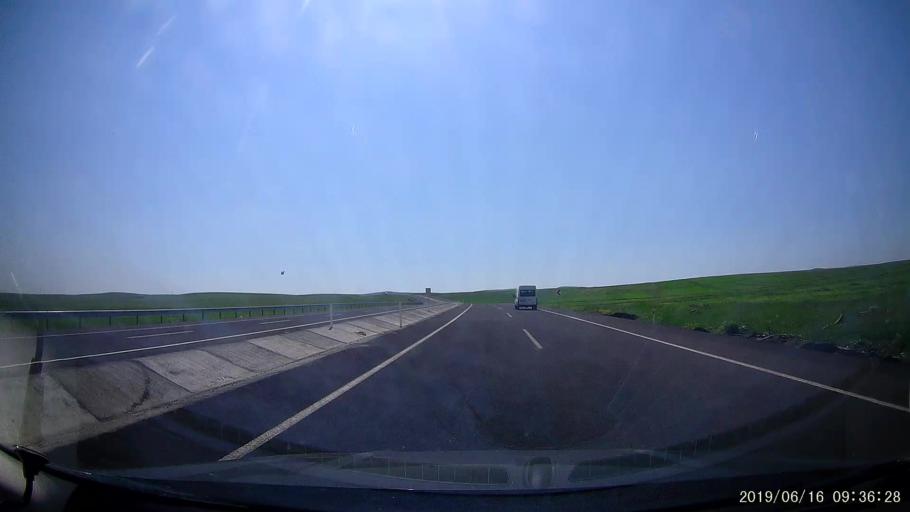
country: TR
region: Kars
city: Kars
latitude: 40.5575
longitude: 43.1737
